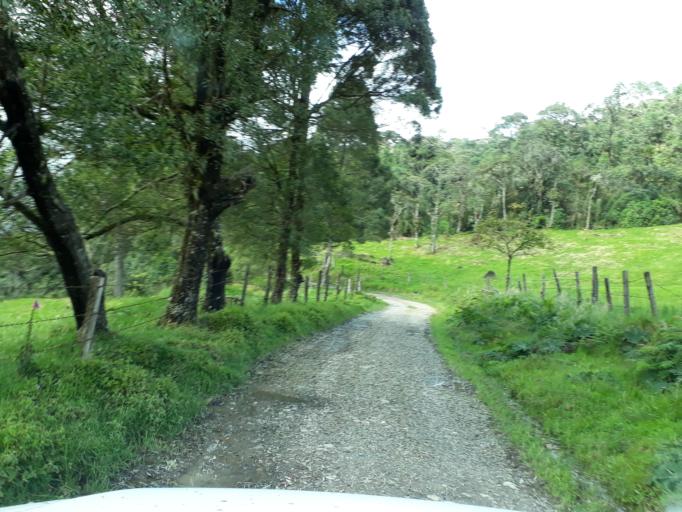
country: CO
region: Cundinamarca
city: Guasca
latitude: 4.8064
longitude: -73.7813
